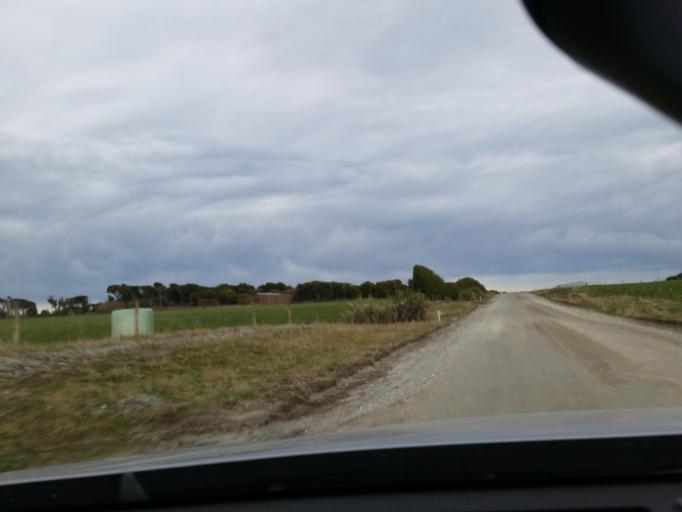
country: NZ
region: Southland
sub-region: Invercargill City
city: Invercargill
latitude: -46.4345
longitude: 168.5062
